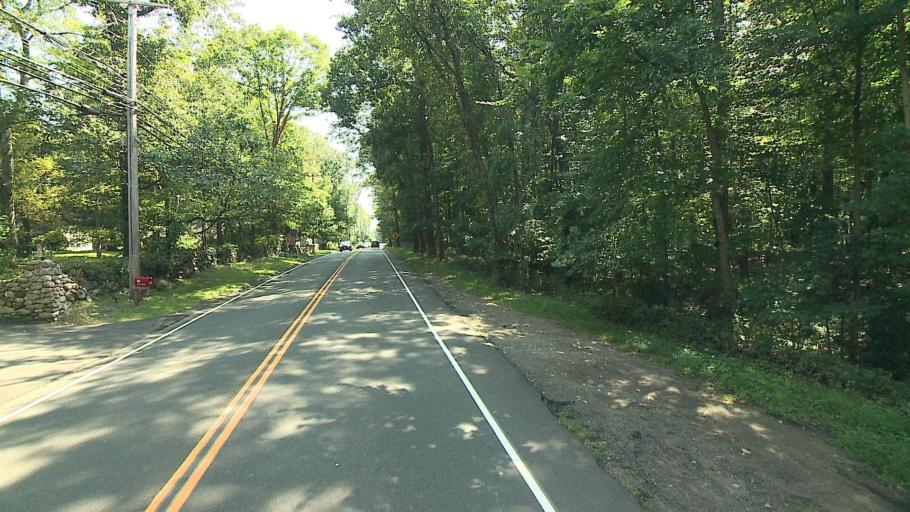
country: US
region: Connecticut
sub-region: Fairfield County
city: Wilton
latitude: 41.1994
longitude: -73.3795
